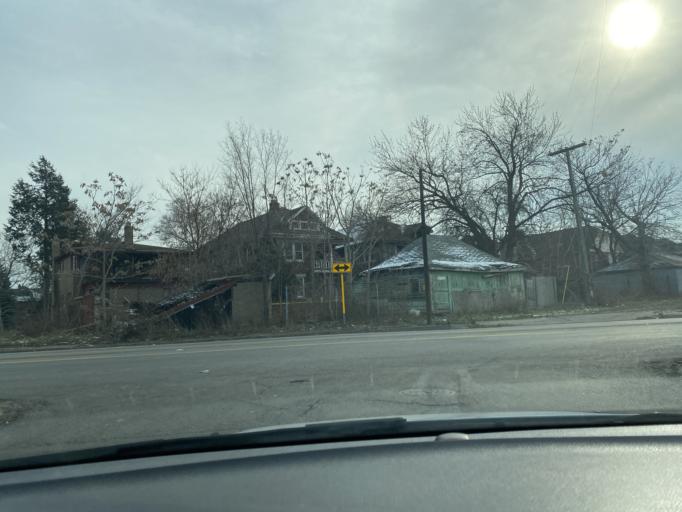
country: US
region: Michigan
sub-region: Wayne County
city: Highland Park
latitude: 42.3664
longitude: -83.1279
